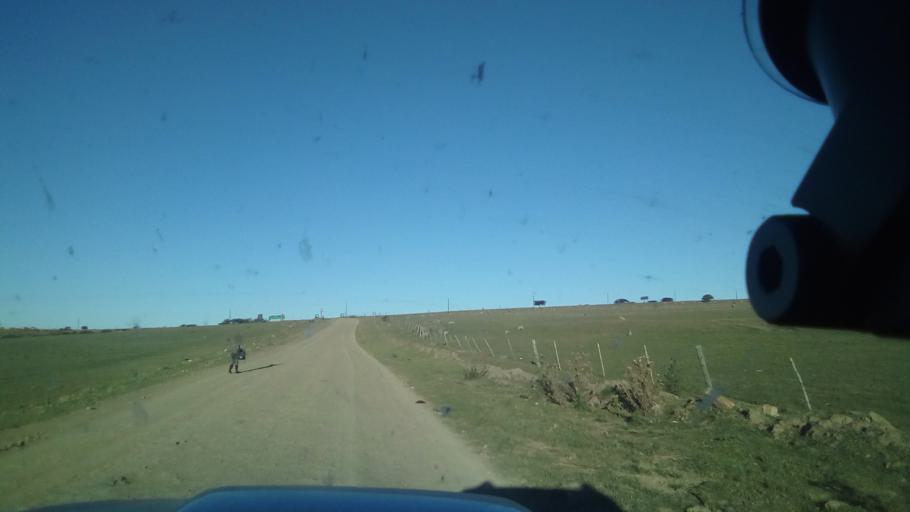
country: ZA
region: Eastern Cape
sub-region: Buffalo City Metropolitan Municipality
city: Bhisho
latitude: -32.9528
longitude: 27.2978
